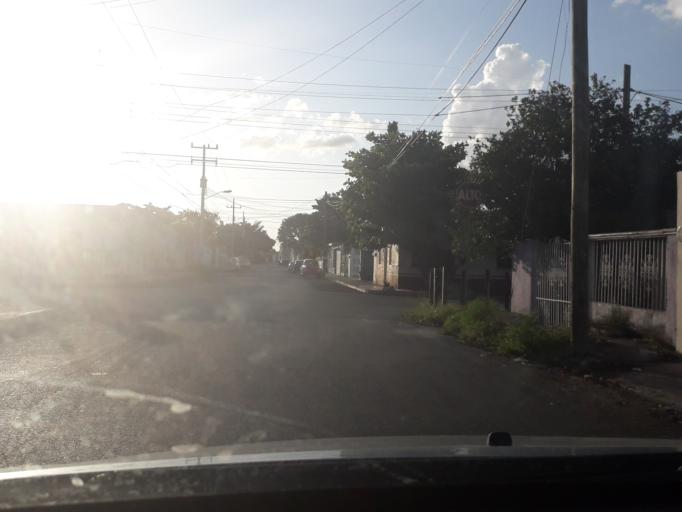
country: MX
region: Yucatan
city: Merida
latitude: 20.9804
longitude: -89.6537
